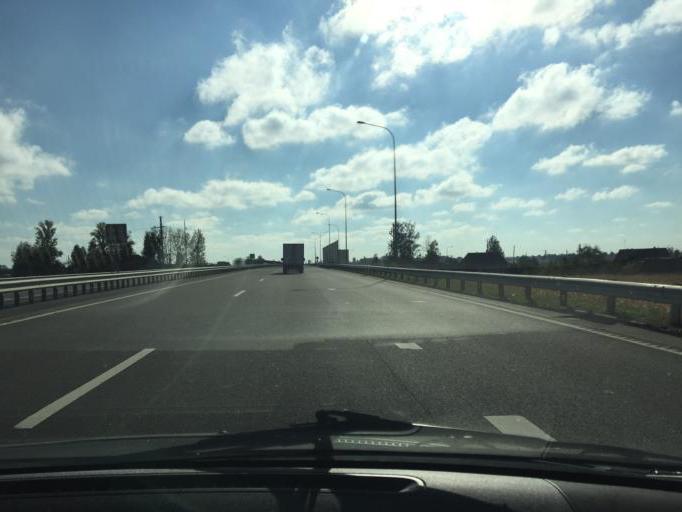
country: BY
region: Minsk
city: Slutsk
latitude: 53.1062
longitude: 27.5687
